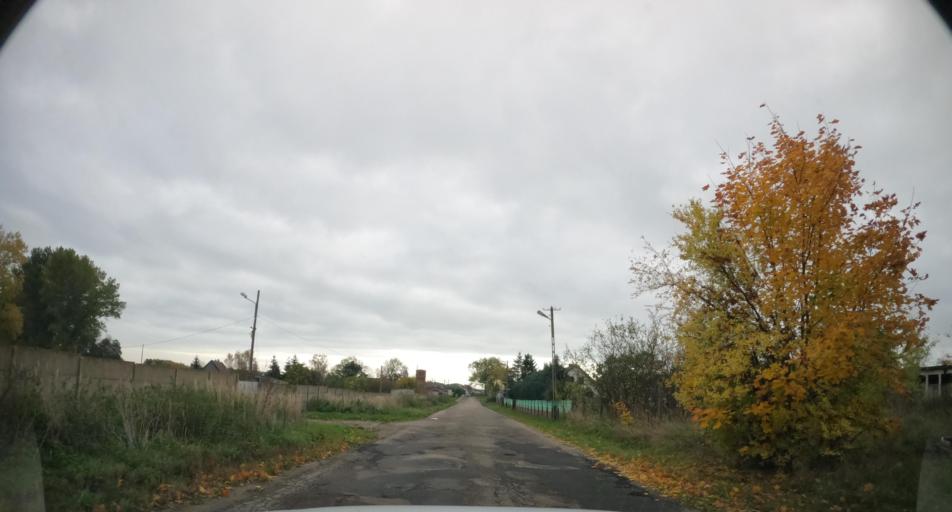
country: PL
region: West Pomeranian Voivodeship
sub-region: Powiat kamienski
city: Wolin
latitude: 53.8671
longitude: 14.5882
